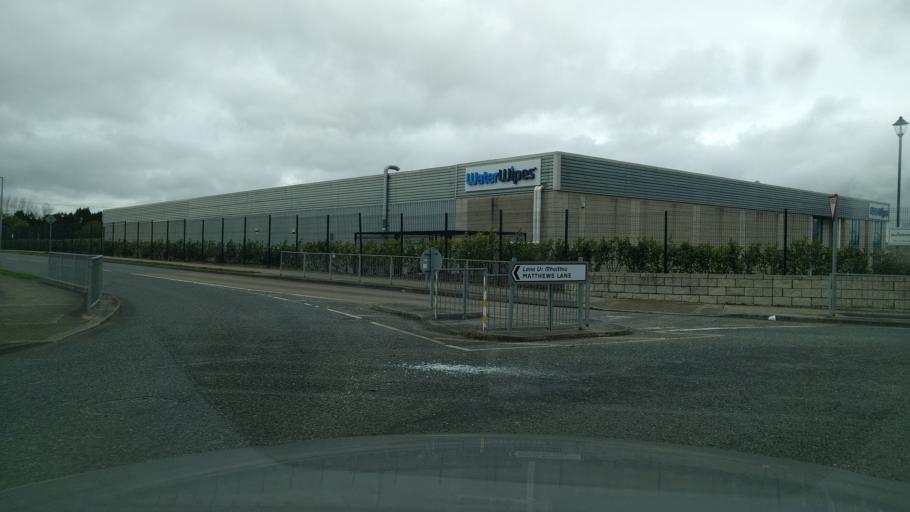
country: IE
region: Leinster
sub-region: Lu
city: Drogheda
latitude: 53.7038
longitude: -6.3693
